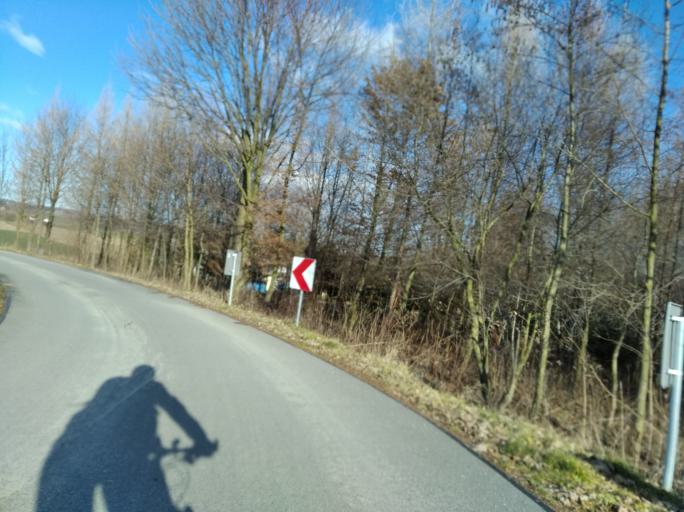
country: PL
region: Subcarpathian Voivodeship
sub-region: Powiat strzyzowski
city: Wisniowa
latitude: 49.9004
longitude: 21.6830
